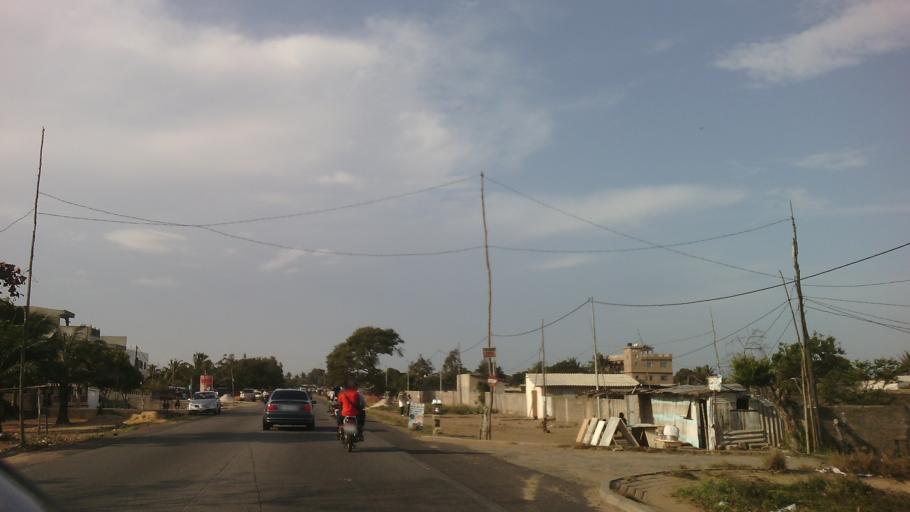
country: TG
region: Maritime
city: Lome
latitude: 6.1855
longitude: 1.3936
